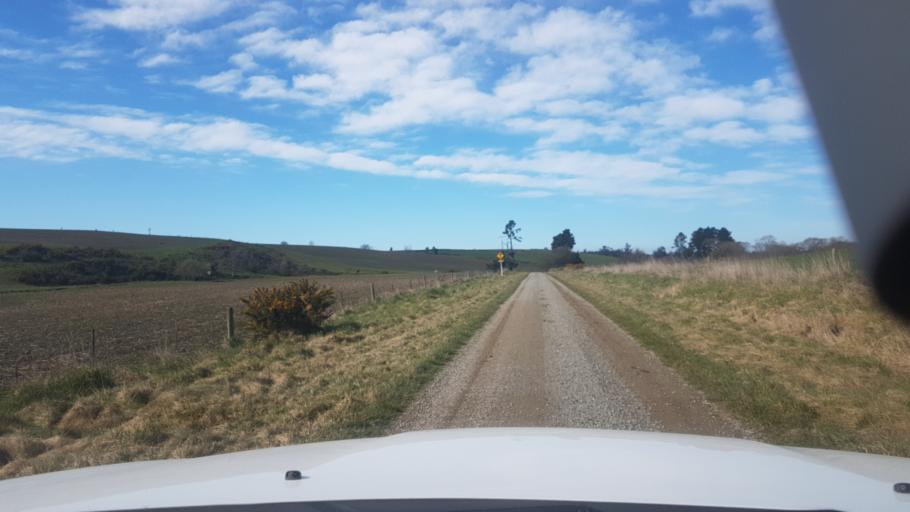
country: NZ
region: Canterbury
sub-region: Timaru District
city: Pleasant Point
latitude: -44.2000
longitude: 171.1792
